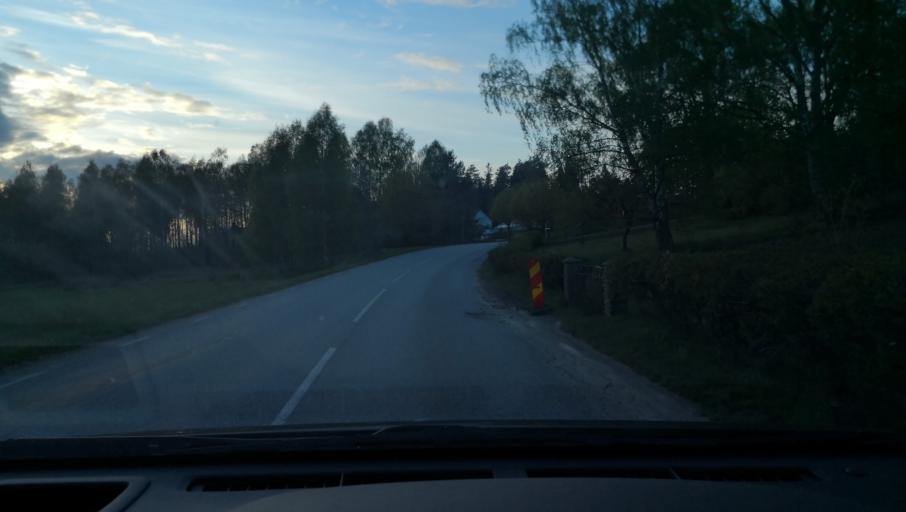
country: SE
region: OErebro
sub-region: Askersunds Kommun
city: Asbro
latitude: 58.9337
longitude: 15.0221
